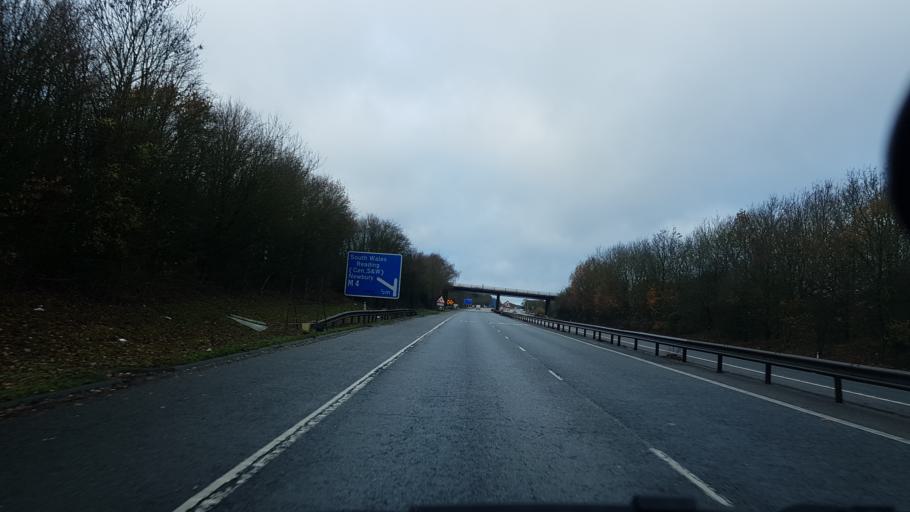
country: GB
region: England
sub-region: Wokingham
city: Wokingham
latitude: 51.4271
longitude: -0.8366
